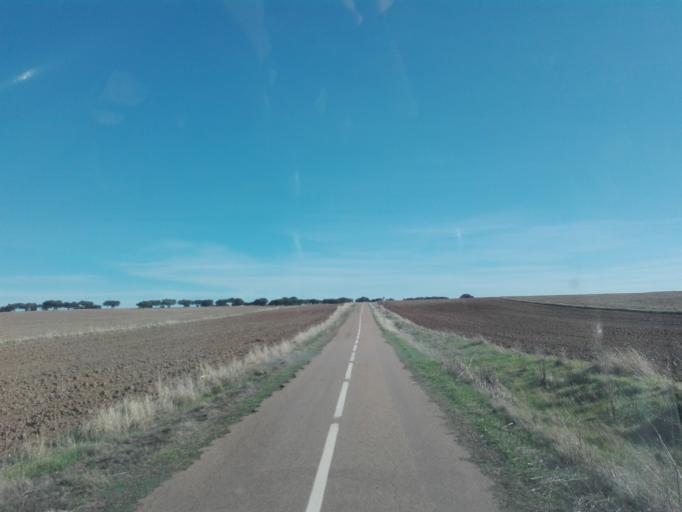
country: ES
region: Extremadura
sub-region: Provincia de Badajoz
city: Valencia de las Torres
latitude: 38.3255
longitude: -5.9574
